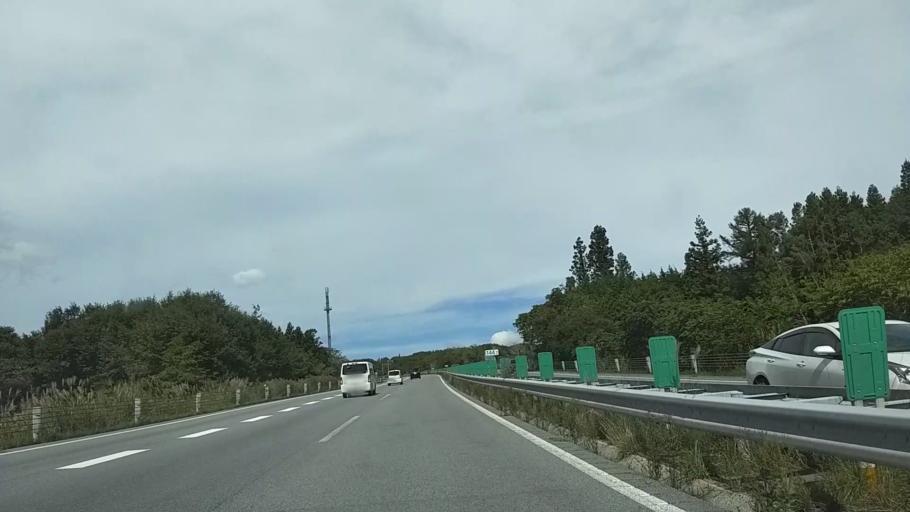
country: JP
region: Yamanashi
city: Nirasaki
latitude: 35.8515
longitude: 138.3437
